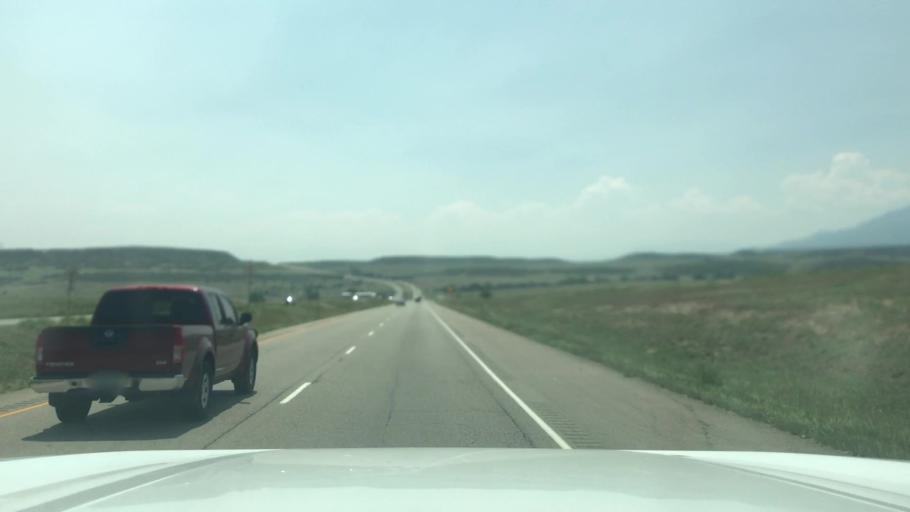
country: US
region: Colorado
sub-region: Pueblo County
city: Colorado City
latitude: 37.9240
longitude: -104.8228
